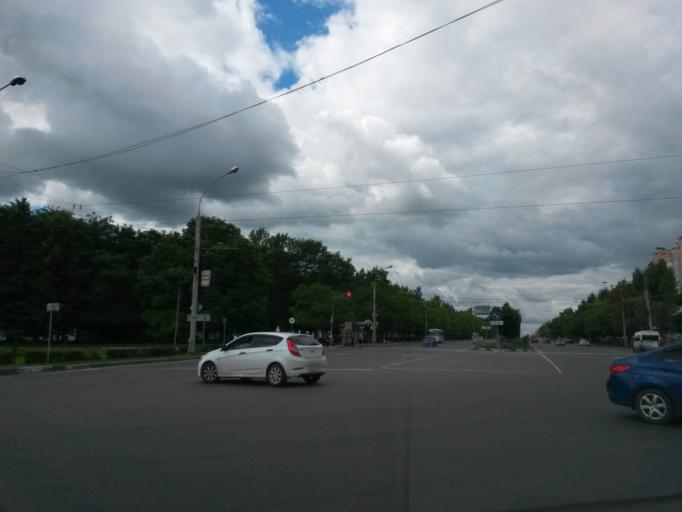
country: RU
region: Jaroslavl
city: Yaroslavl
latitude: 57.6857
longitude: 39.7850
